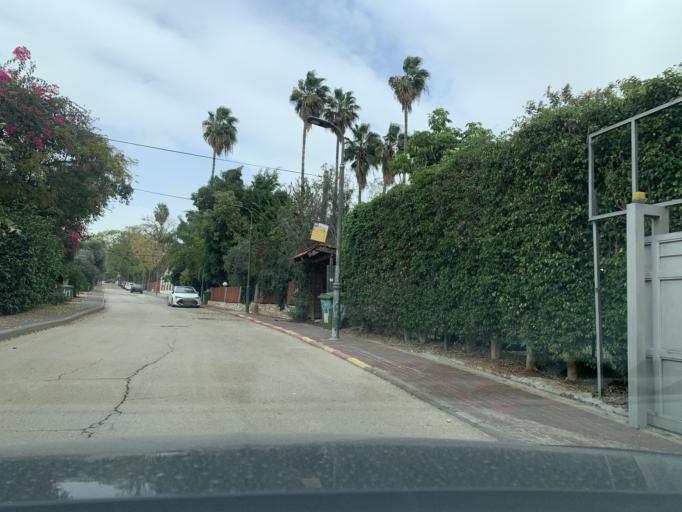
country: IL
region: Central District
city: Jaljulya
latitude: 32.1582
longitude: 34.9463
